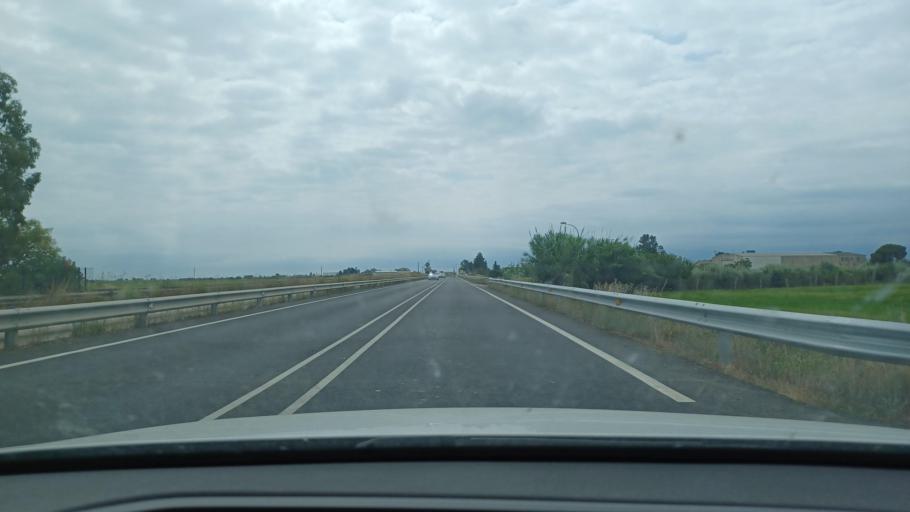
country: ES
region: Catalonia
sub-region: Provincia de Tarragona
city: Deltebre
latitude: 40.7164
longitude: 0.7515
